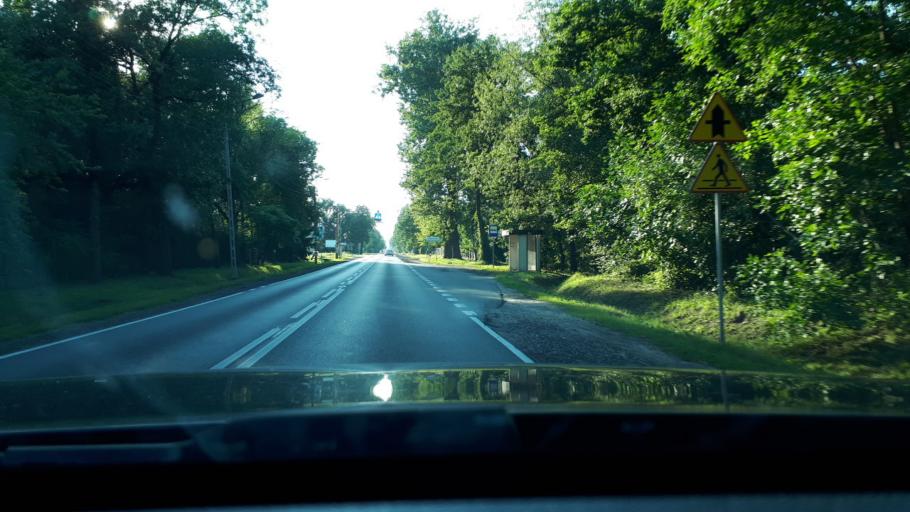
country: PL
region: Masovian Voivodeship
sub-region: Powiat piaseczynski
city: Baniocha
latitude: 52.0092
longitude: 21.1556
